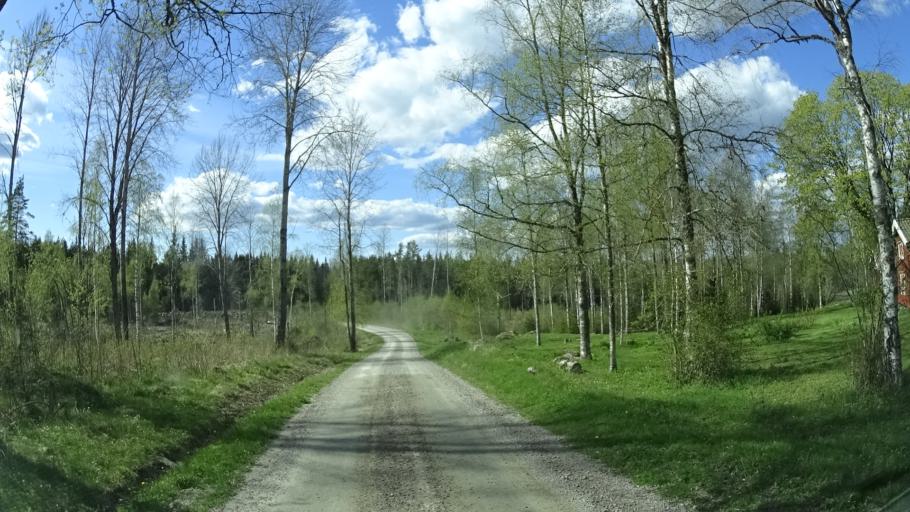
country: SE
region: OErebro
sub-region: Orebro Kommun
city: Garphyttan
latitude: 59.4259
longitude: 14.8662
